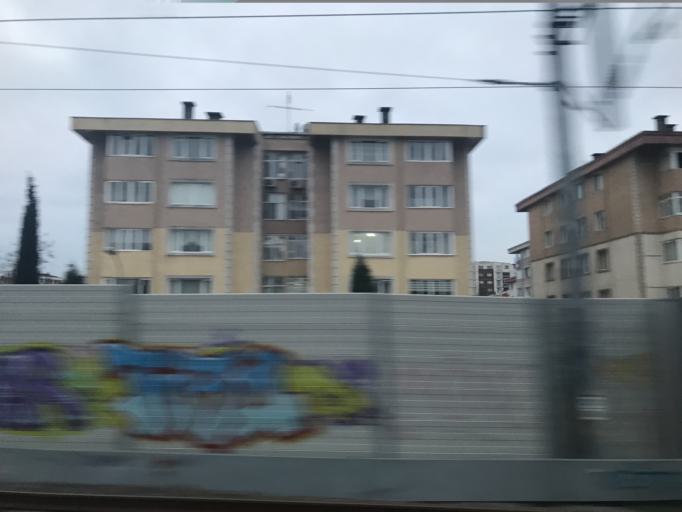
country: TR
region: Istanbul
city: Icmeler
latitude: 40.8357
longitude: 29.3137
